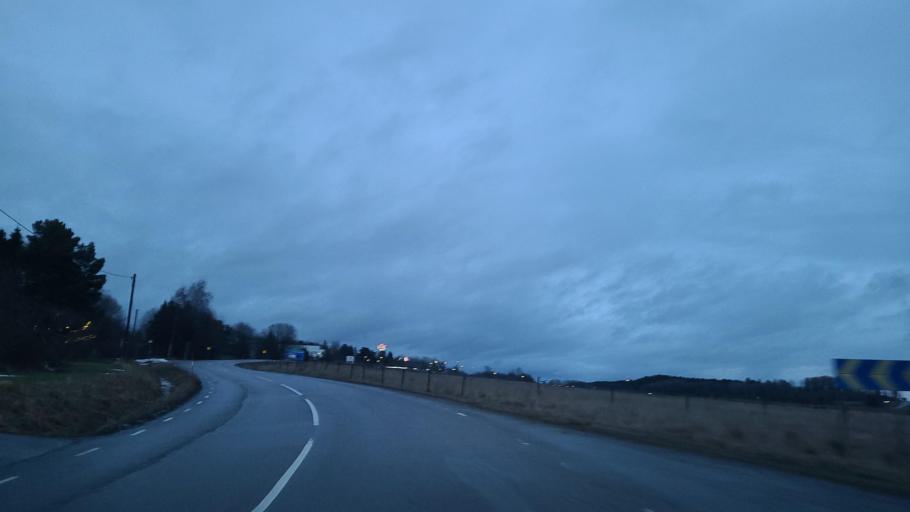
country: SE
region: Stockholm
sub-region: Norrtalje Kommun
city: Norrtalje
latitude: 59.7423
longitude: 18.6759
